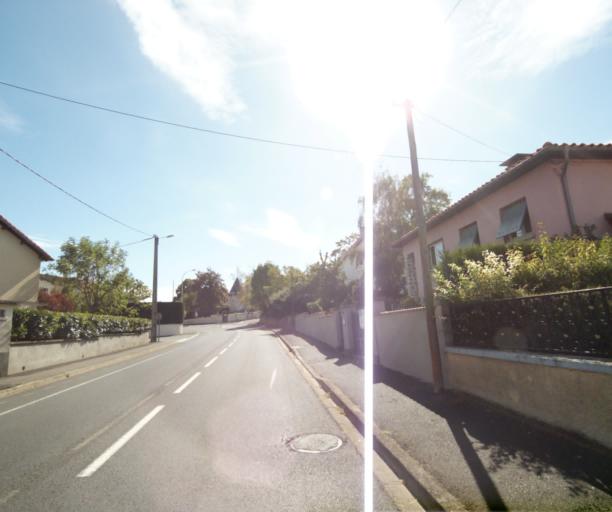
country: FR
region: Auvergne
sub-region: Departement du Puy-de-Dome
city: Cournon-d'Auvergne
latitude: 45.7665
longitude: 3.1997
